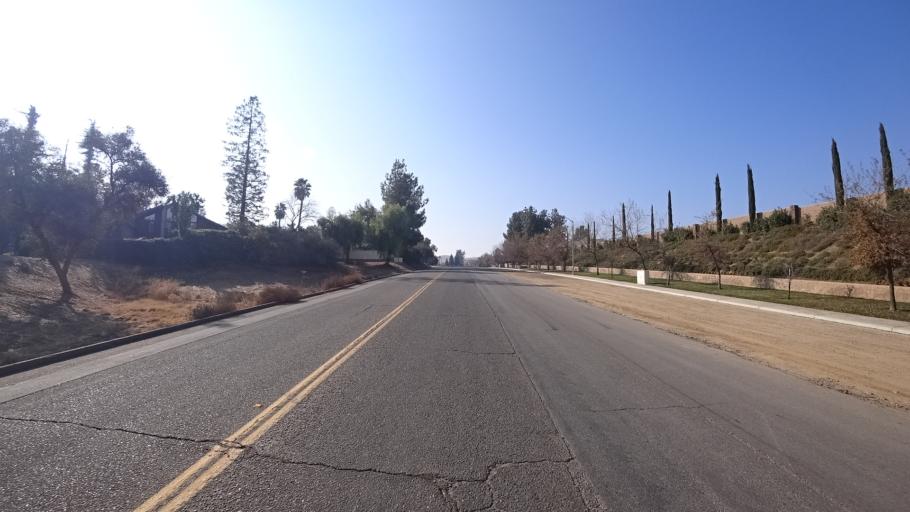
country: US
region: California
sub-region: Kern County
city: Oildale
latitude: 35.4325
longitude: -118.8666
